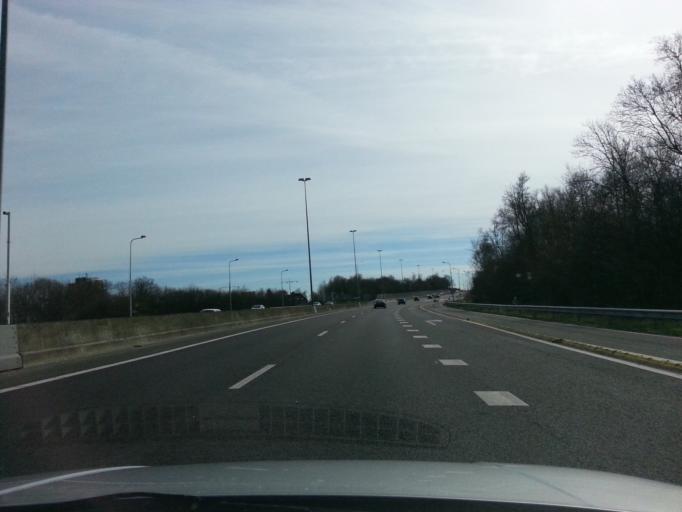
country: NL
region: Groningen
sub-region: Gemeente Haren
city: Haren
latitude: 53.1719
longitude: 6.5893
